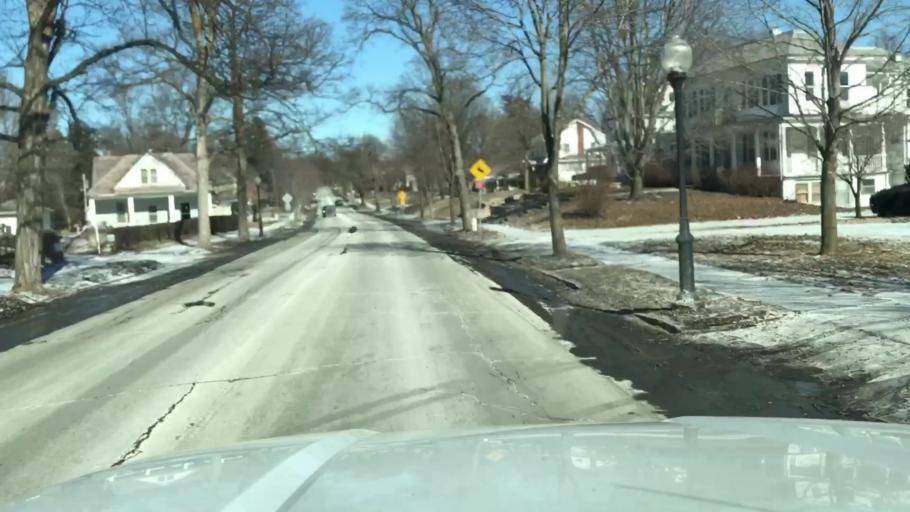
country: US
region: Missouri
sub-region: Buchanan County
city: Saint Joseph
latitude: 39.7872
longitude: -94.8219
